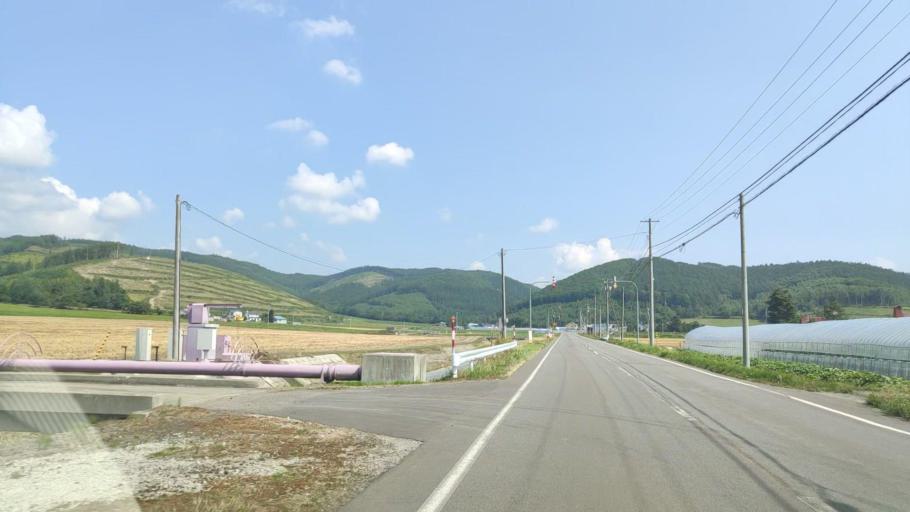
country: JP
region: Hokkaido
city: Shimo-furano
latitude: 43.4131
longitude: 142.3987
